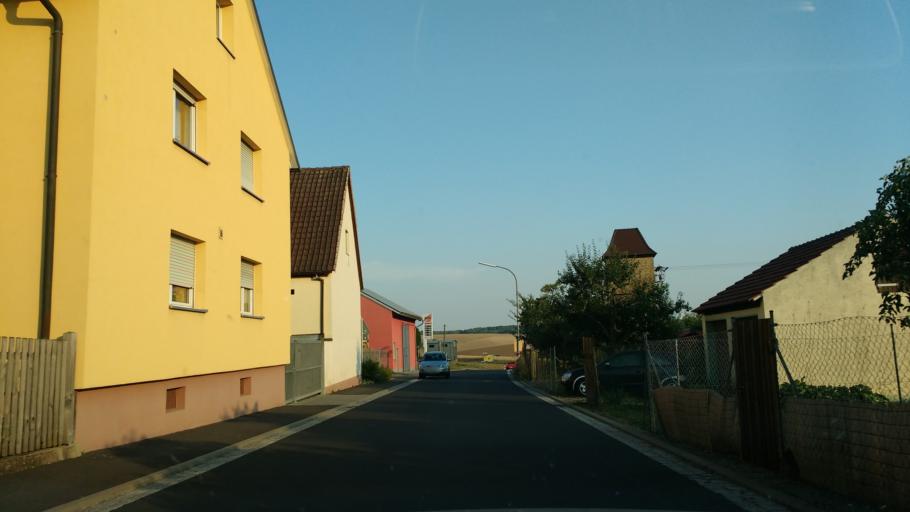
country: DE
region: Bavaria
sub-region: Regierungsbezirk Unterfranken
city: Wasserlosen
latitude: 50.0758
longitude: 10.0399
